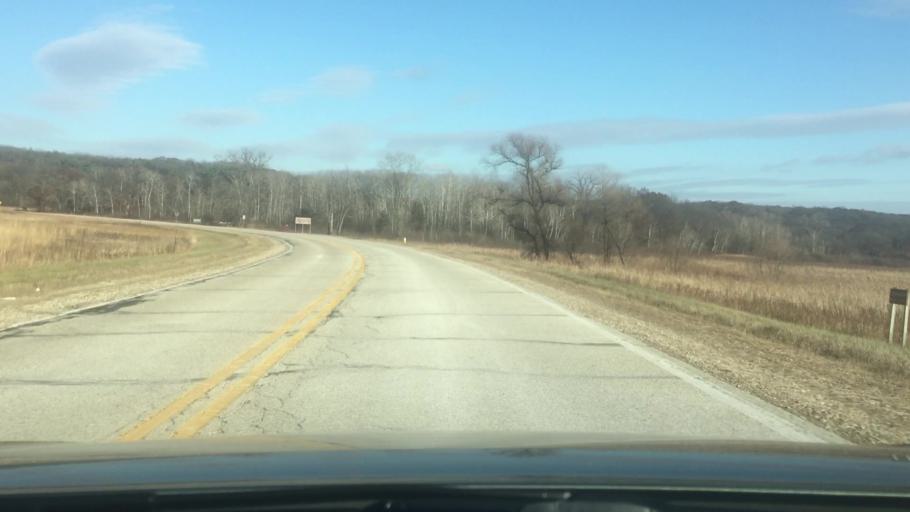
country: US
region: Wisconsin
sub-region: Waukesha County
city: Eagle
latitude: 42.9345
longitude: -88.4770
